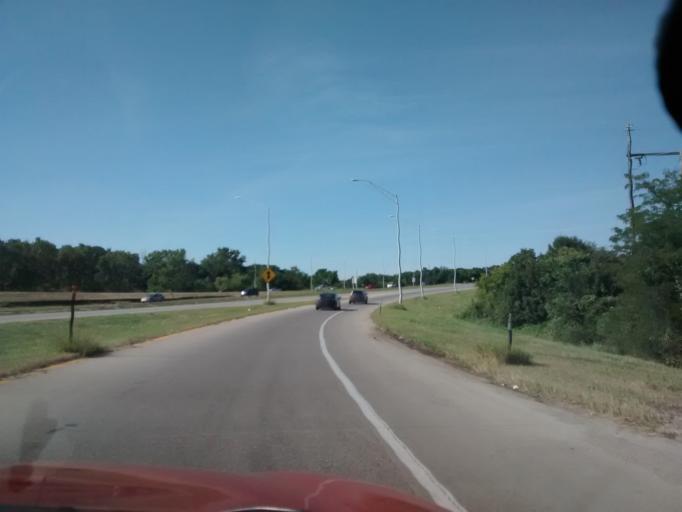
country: US
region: Nebraska
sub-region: Sarpy County
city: Offutt Air Force Base
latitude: 41.1599
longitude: -95.9382
